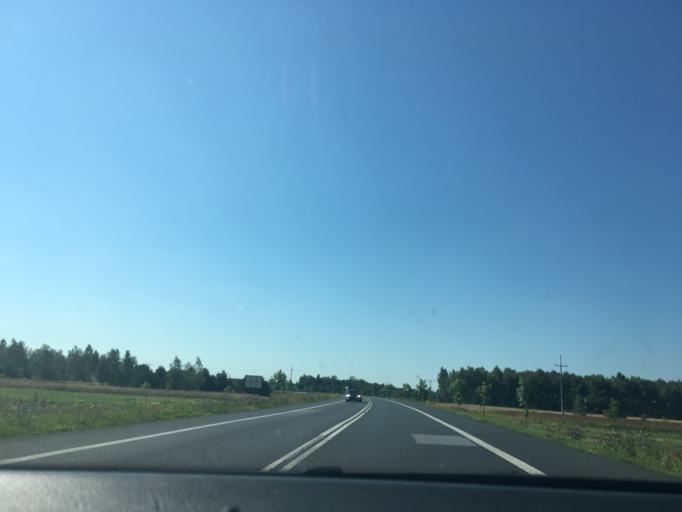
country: PL
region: Lublin Voivodeship
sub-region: Powiat lubartowski
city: Lubartow
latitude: 51.4597
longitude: 22.5757
